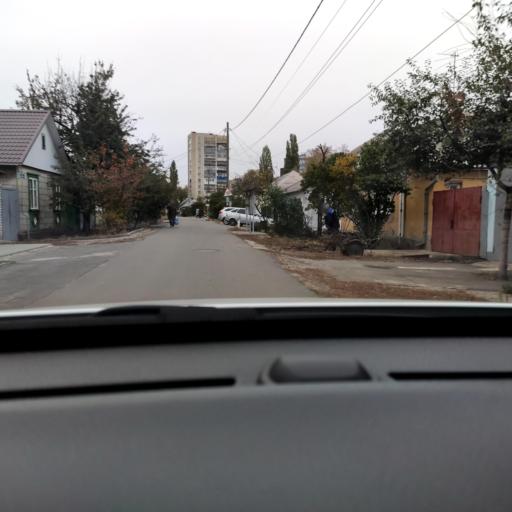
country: RU
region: Voronezj
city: Voronezh
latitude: 51.6589
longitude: 39.2750
